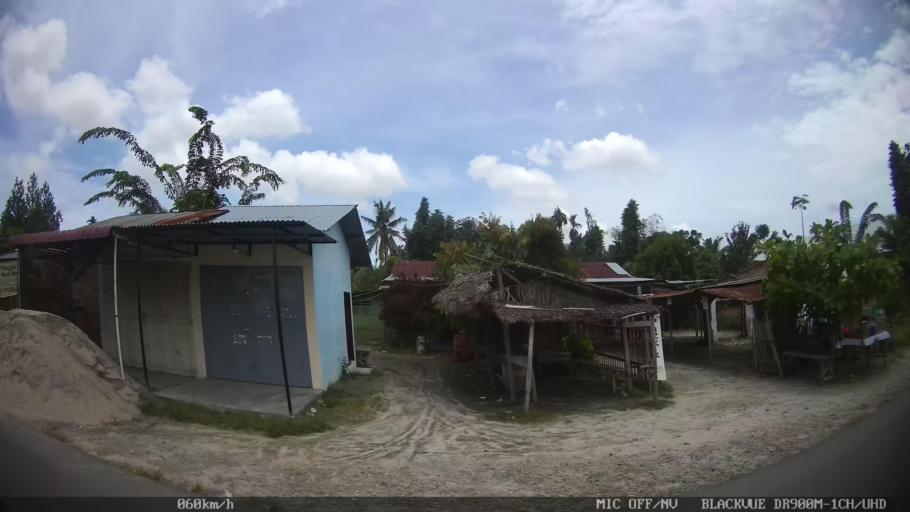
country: ID
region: North Sumatra
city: Percut
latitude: 3.5789
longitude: 98.8833
